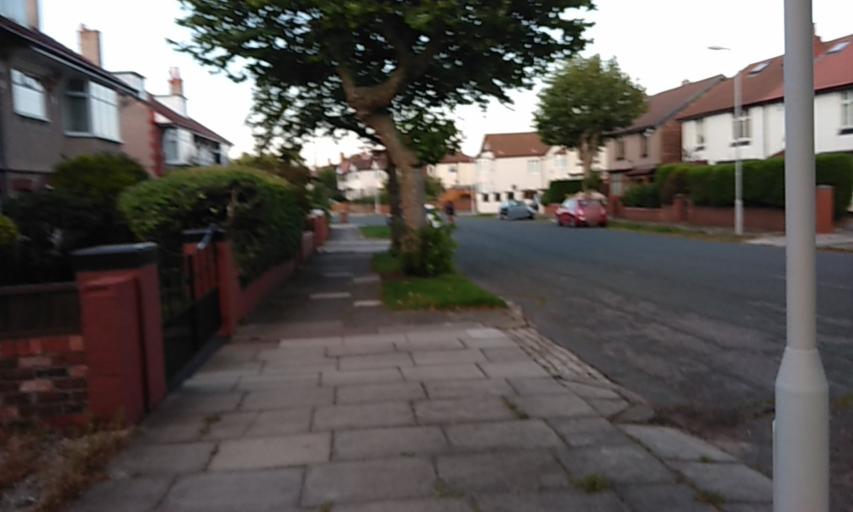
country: GB
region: England
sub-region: Metropolitan Borough of Wirral
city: Wallasey
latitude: 53.4226
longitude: -3.0583
